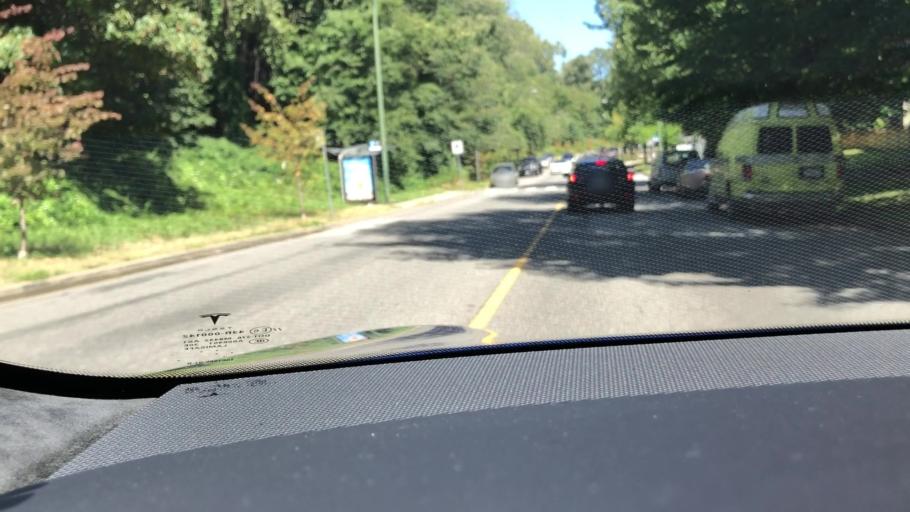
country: CA
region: British Columbia
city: Vancouver
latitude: 49.2084
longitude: -123.0363
